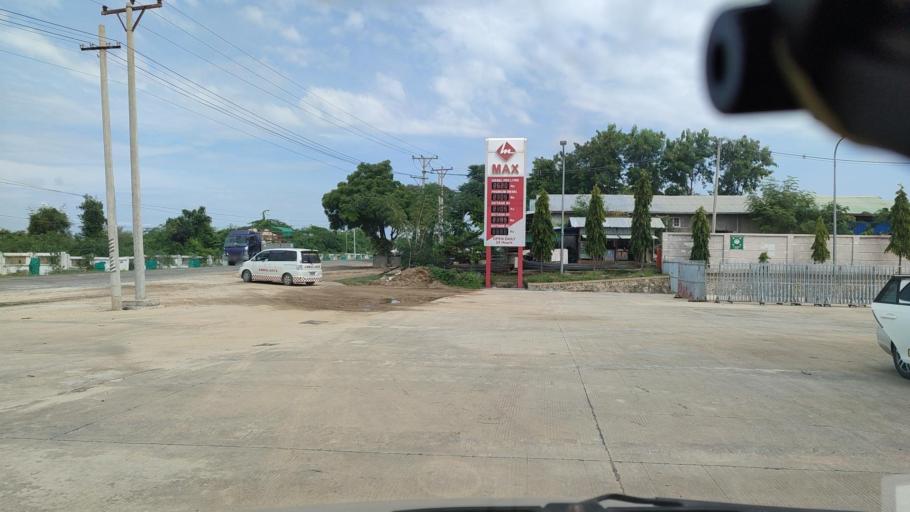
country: MM
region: Mandalay
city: Meiktila
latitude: 20.9128
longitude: 95.8479
